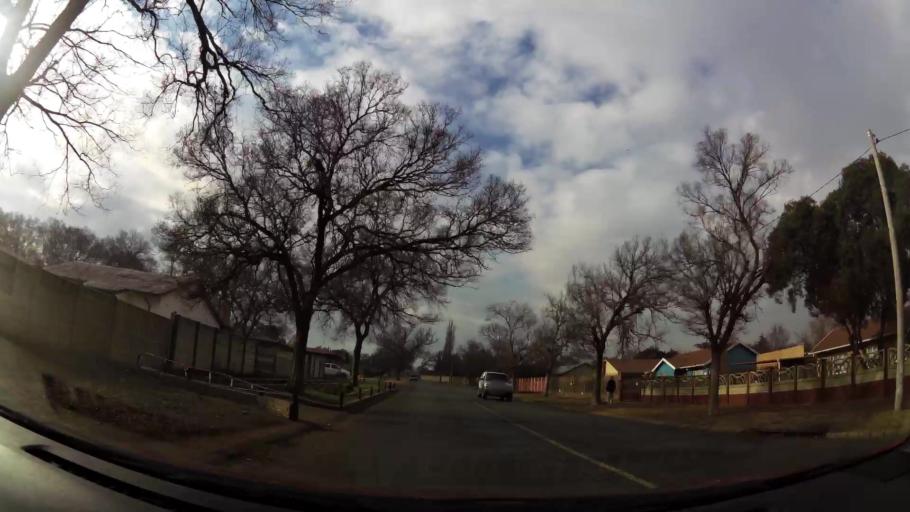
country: ZA
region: Gauteng
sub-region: Sedibeng District Municipality
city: Vanderbijlpark
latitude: -26.7053
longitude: 27.8192
